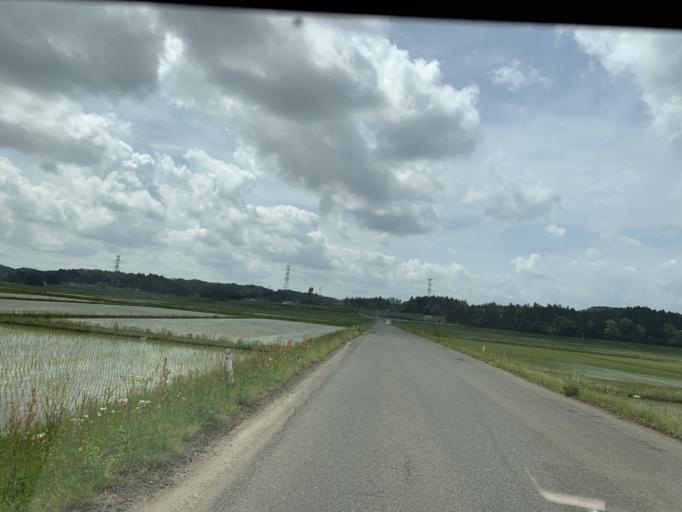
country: JP
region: Iwate
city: Ichinoseki
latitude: 38.8217
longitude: 141.0202
